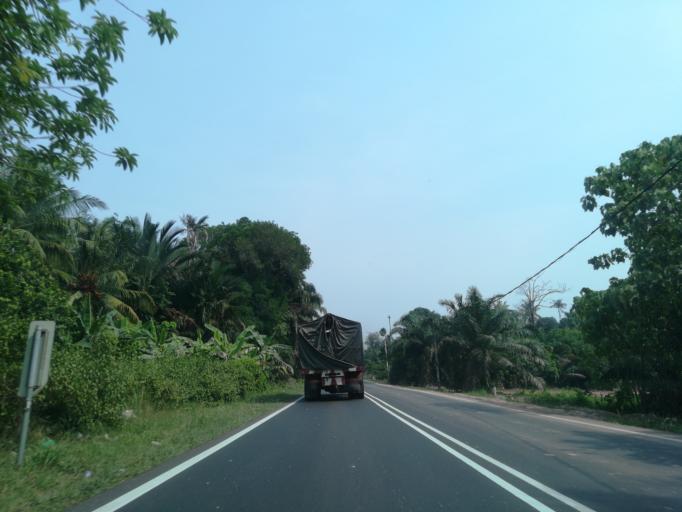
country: MY
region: Penang
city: Tasek Glugor
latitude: 5.4504
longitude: 100.5488
